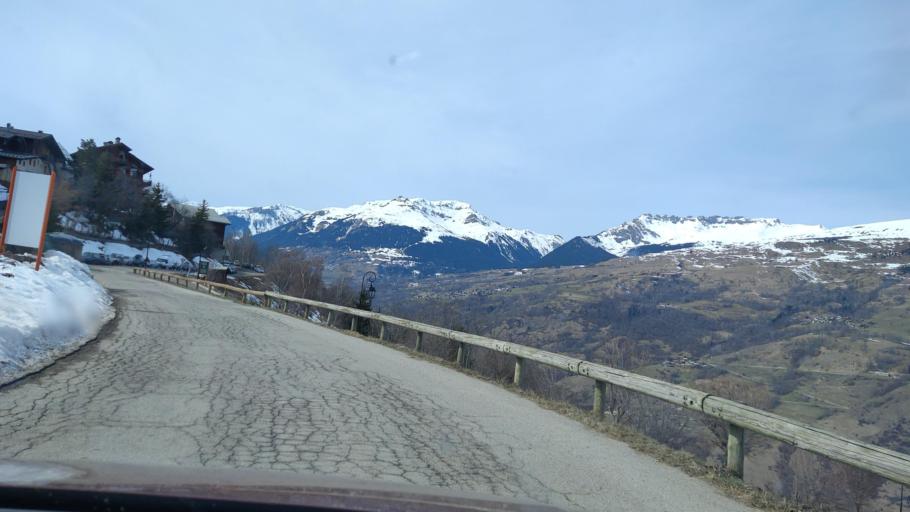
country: FR
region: Rhone-Alpes
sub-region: Departement de la Savoie
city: Belle-Plagne
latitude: 45.5607
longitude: 6.7389
